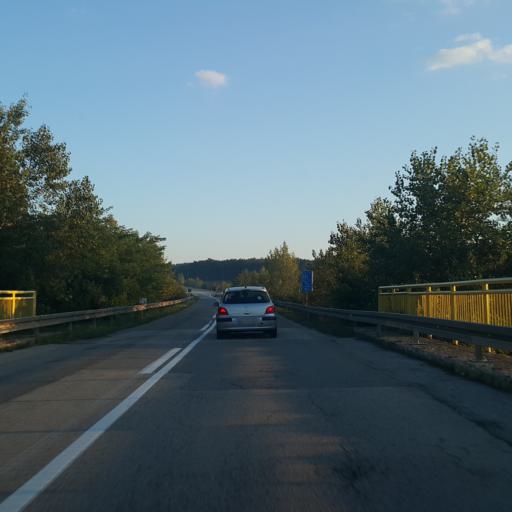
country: RS
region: Central Serbia
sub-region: Zajecarski Okrug
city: Zajecar
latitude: 44.0991
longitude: 22.3478
